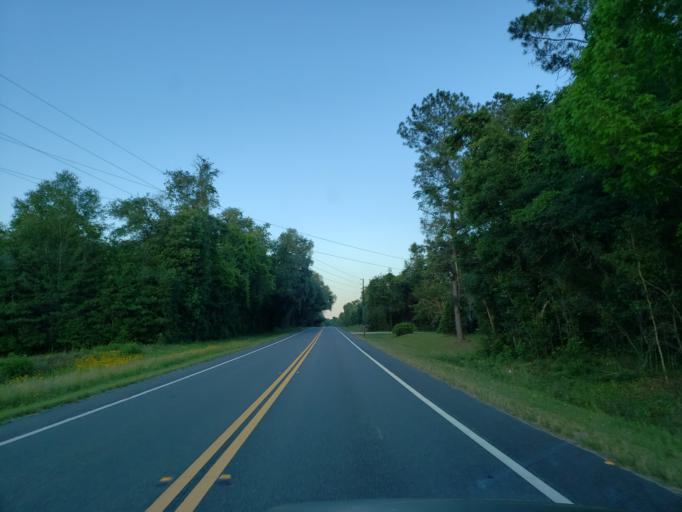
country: US
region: Florida
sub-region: Madison County
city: Madison
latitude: 30.5813
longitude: -83.2216
